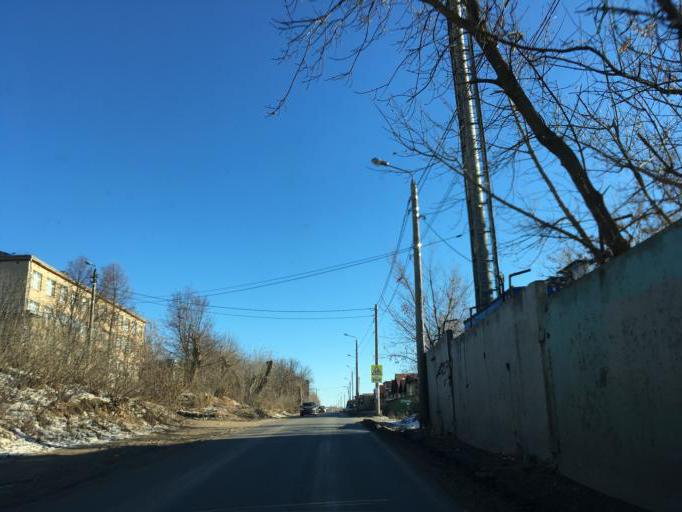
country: RU
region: Tula
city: Tula
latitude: 54.1940
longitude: 37.6668
